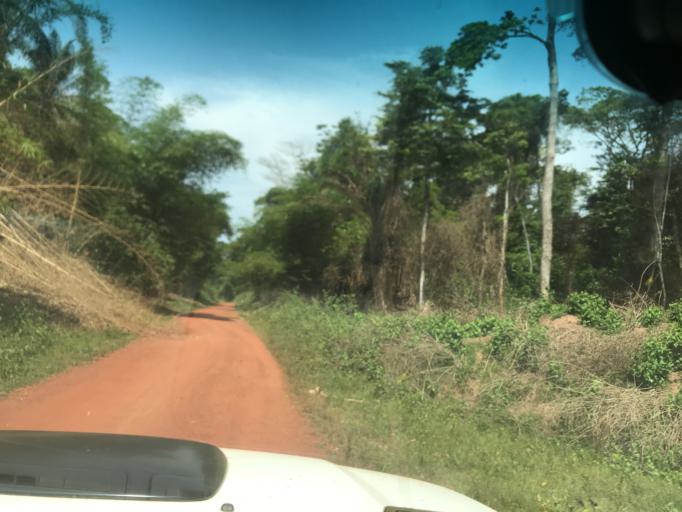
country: CD
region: Eastern Province
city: Aketi
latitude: 2.8877
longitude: 23.9813
